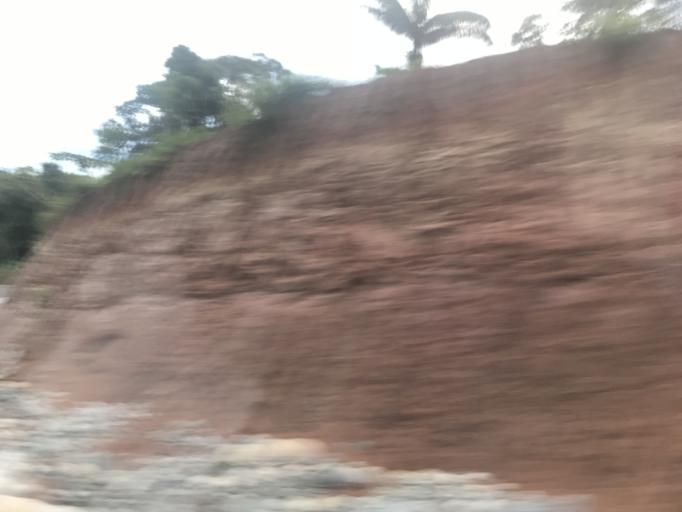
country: EC
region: Napo
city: Tena
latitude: -1.0575
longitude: -77.6998
